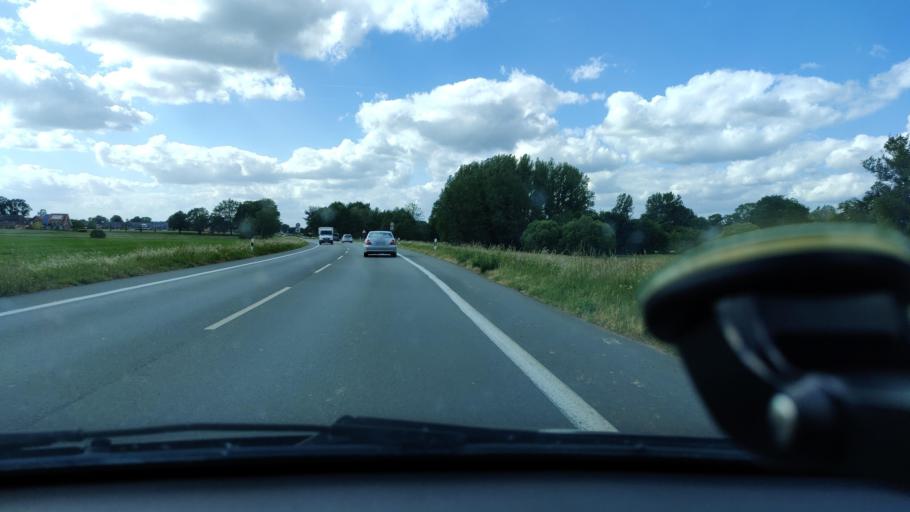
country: DE
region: North Rhine-Westphalia
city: Stadtlohn
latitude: 51.9785
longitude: 6.9583
